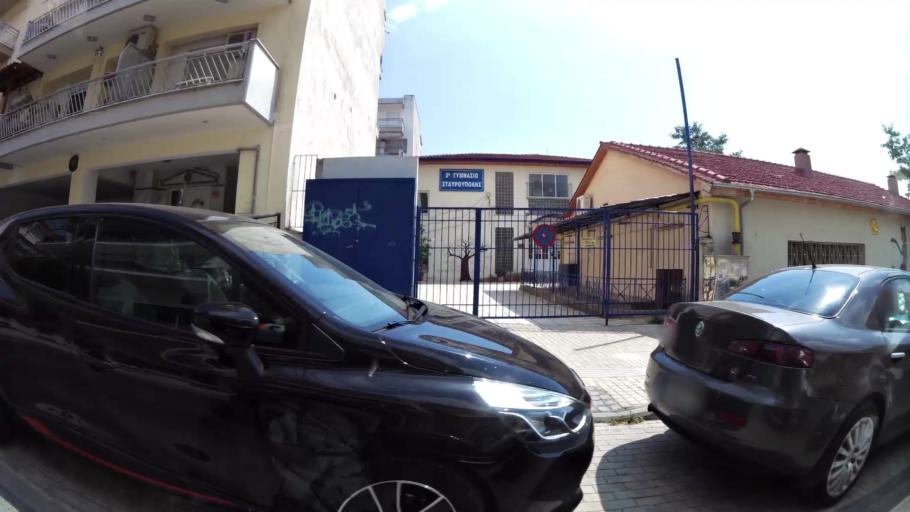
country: GR
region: Central Macedonia
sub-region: Nomos Thessalonikis
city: Stavroupoli
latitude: 40.6641
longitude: 22.9400
